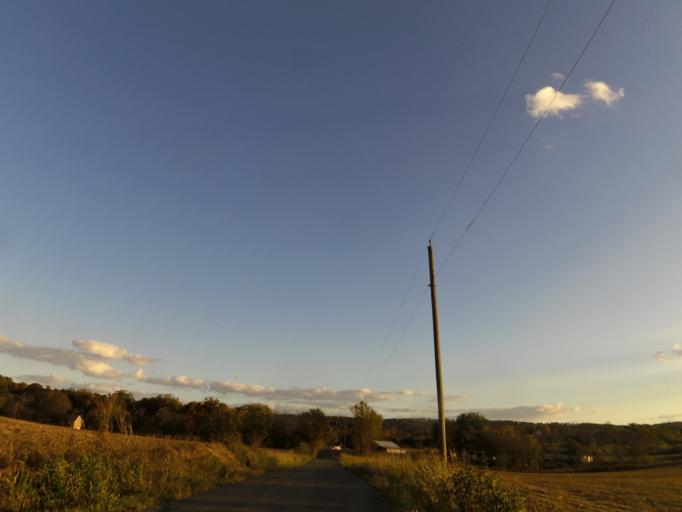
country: US
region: Tennessee
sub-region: Sevier County
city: Seymour
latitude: 35.9502
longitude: -83.7253
